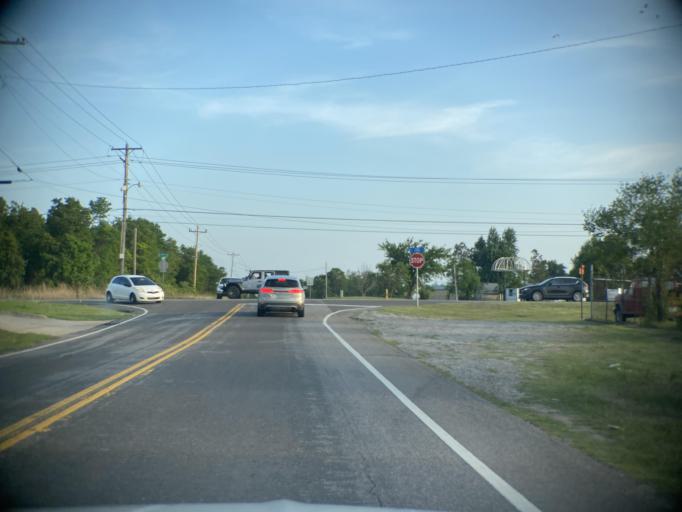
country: US
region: Oklahoma
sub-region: Oklahoma County
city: Nicoma Park
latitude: 35.4360
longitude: -97.3357
